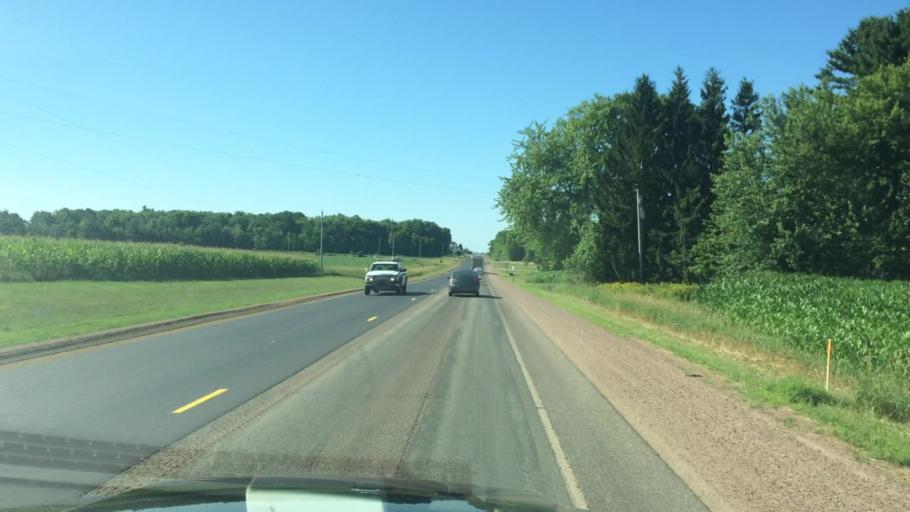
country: US
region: Wisconsin
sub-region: Marathon County
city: Stratford
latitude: 44.8623
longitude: -90.0791
